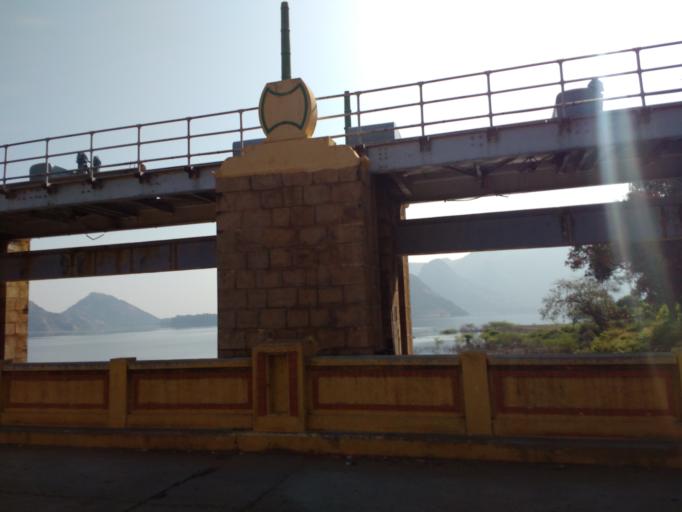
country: IN
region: Tamil Nadu
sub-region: Tiruppur
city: Dhali
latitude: 10.4750
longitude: 77.1485
